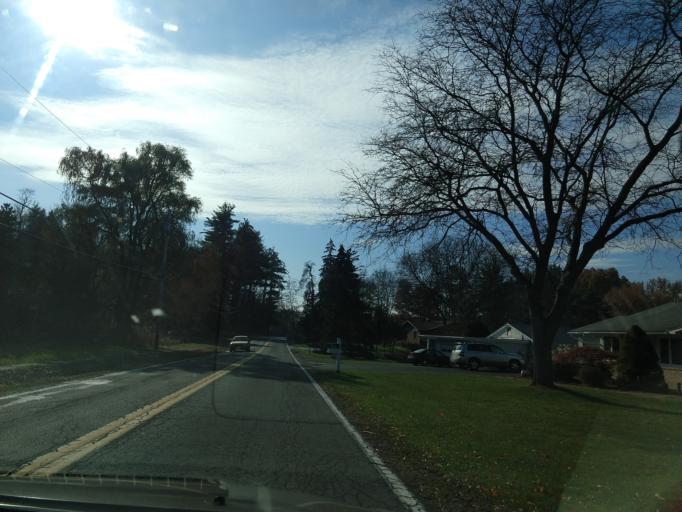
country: US
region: New York
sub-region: Tompkins County
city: Cayuga Heights
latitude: 42.4677
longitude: -76.4814
